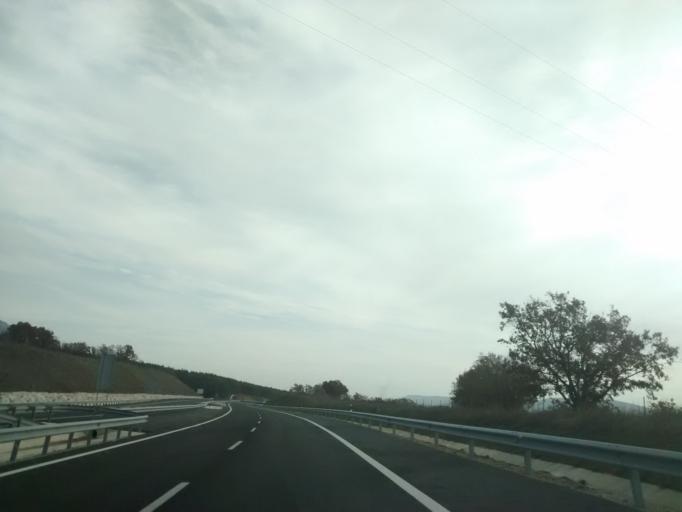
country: ES
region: Navarre
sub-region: Provincia de Navarra
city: Yesa
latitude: 42.6215
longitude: -1.1621
